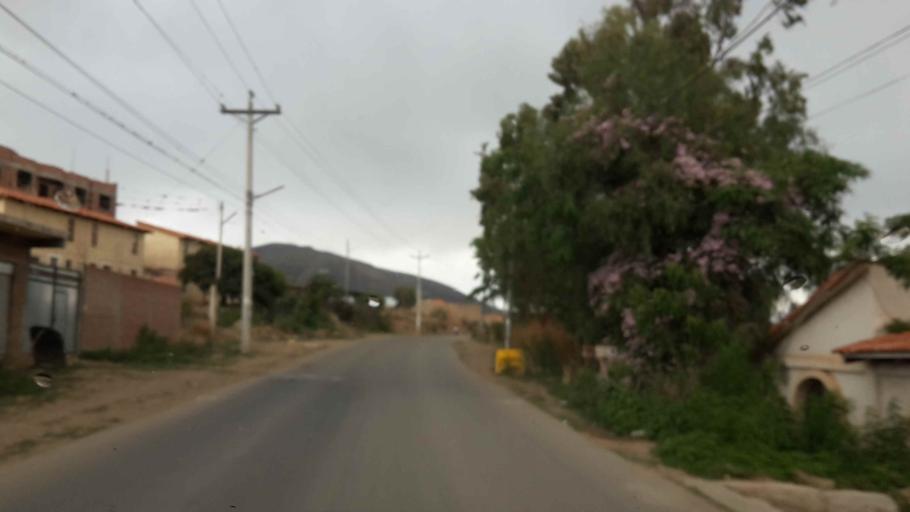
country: BO
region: Cochabamba
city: Tarata
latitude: -17.6087
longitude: -66.0269
